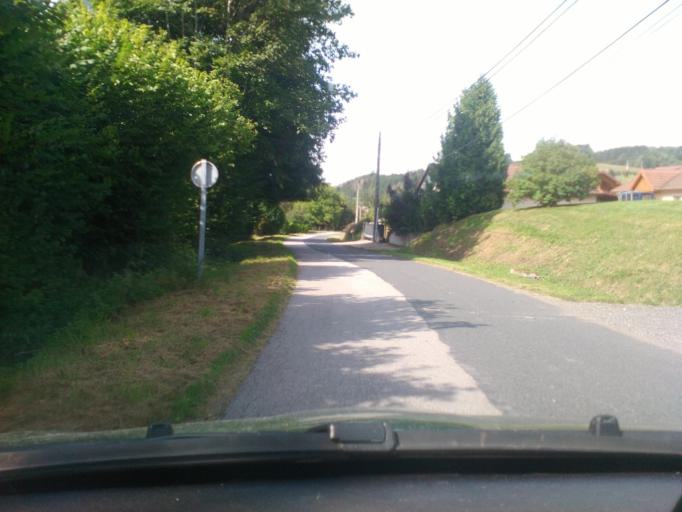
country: FR
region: Lorraine
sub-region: Departement des Vosges
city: Fraize
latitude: 48.2145
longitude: 7.0118
